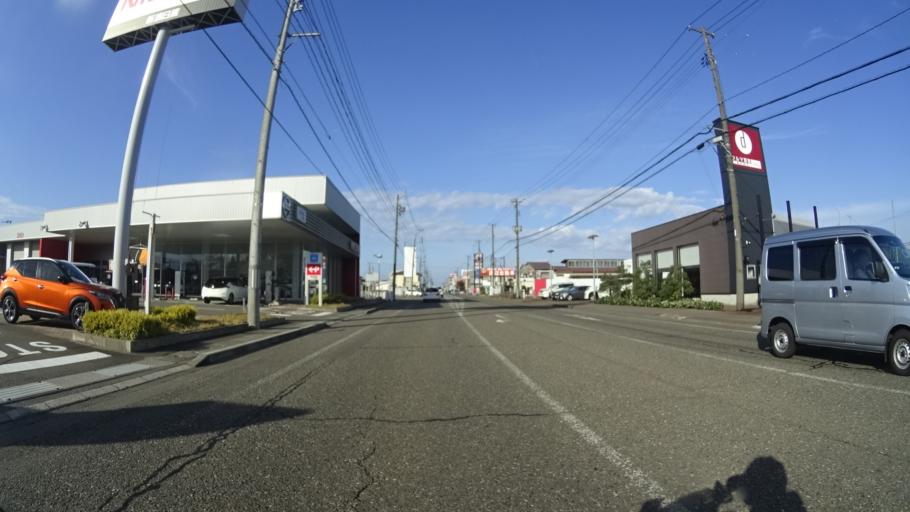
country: JP
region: Niigata
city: Joetsu
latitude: 37.1540
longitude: 138.2383
